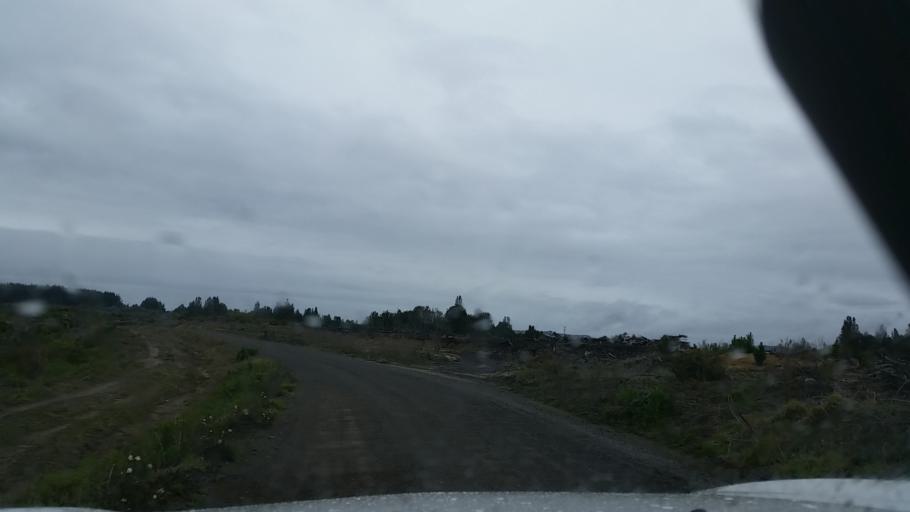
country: NZ
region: Bay of Plenty
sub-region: Kawerau District
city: Kawerau
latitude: -37.9980
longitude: 176.5404
